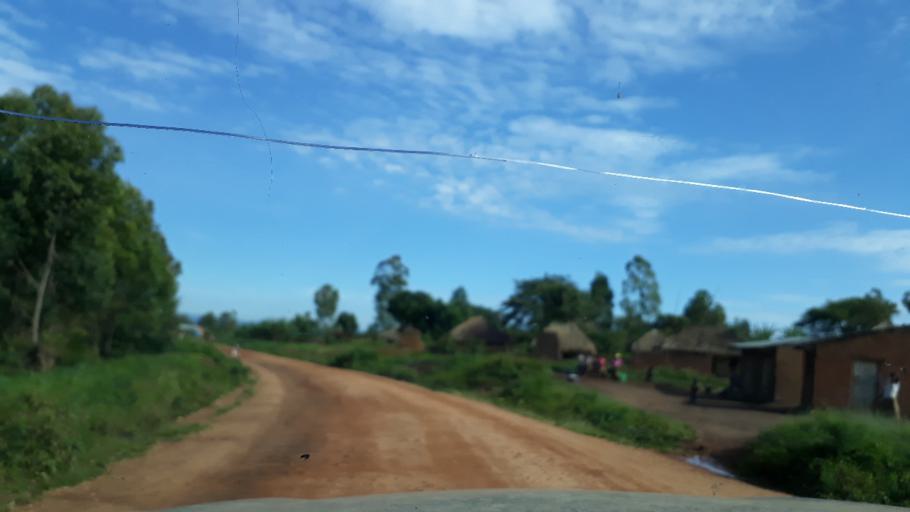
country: UG
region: Northern Region
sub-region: Zombo District
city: Paidha
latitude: 2.3360
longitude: 31.0272
